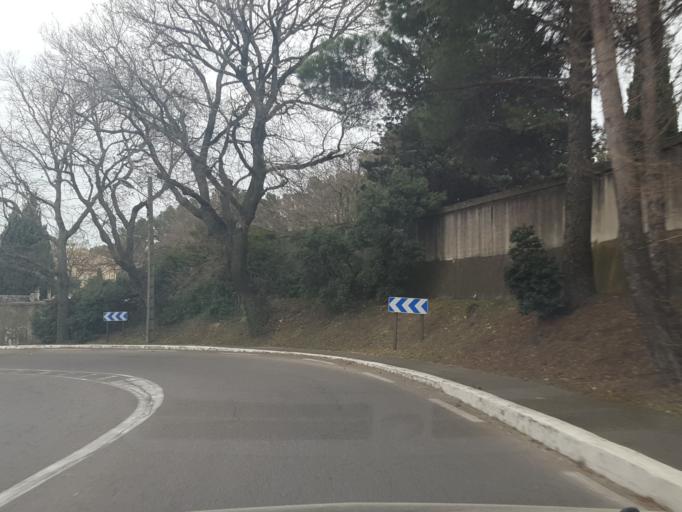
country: FR
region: Provence-Alpes-Cote d'Azur
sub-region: Departement du Vaucluse
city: Chateauneuf-de-Gadagne
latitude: 43.9260
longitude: 4.9402
